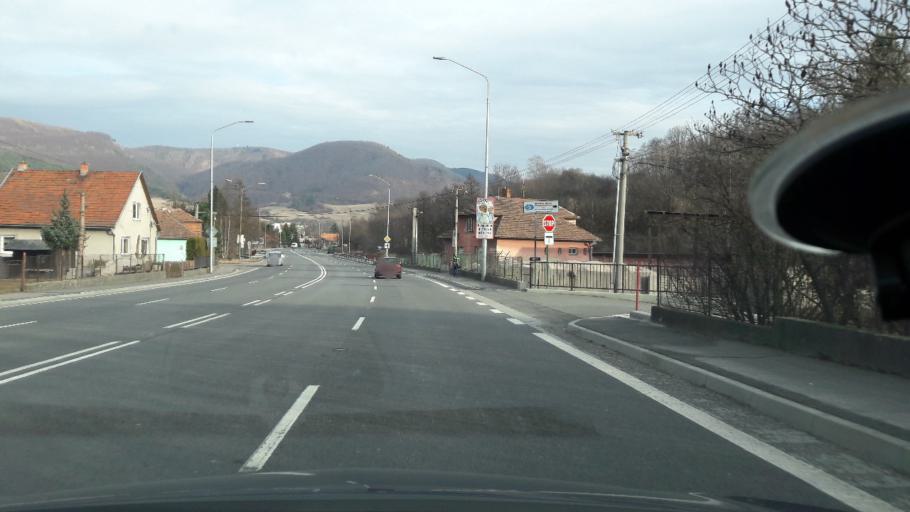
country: SK
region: Nitriansky
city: Handlova
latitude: 48.7713
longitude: 18.7457
